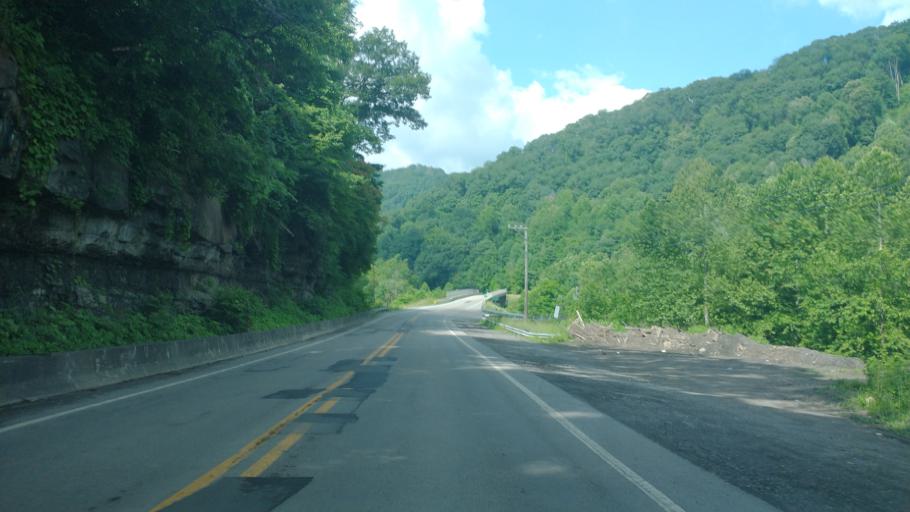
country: US
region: West Virginia
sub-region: McDowell County
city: Welch
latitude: 37.4094
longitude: -81.4590
